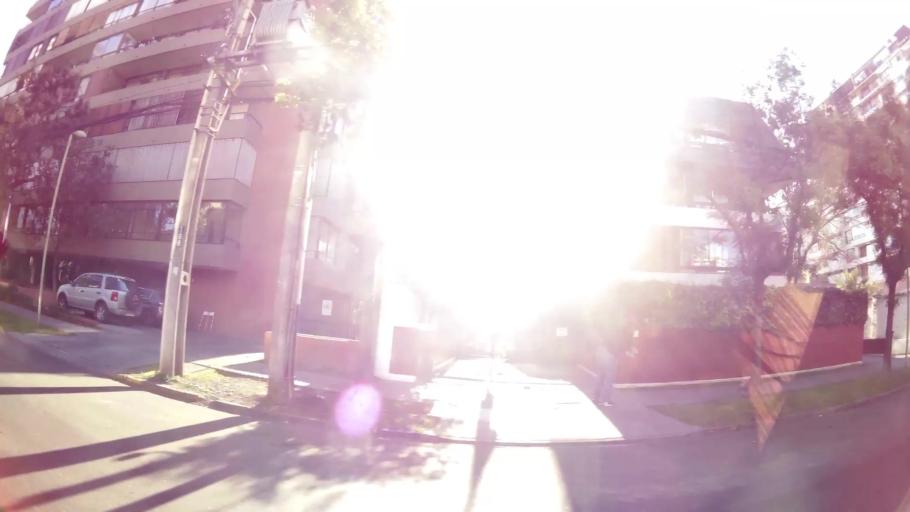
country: CL
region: Santiago Metropolitan
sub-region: Provincia de Santiago
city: Villa Presidente Frei, Nunoa, Santiago, Chile
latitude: -33.4256
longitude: -70.5854
